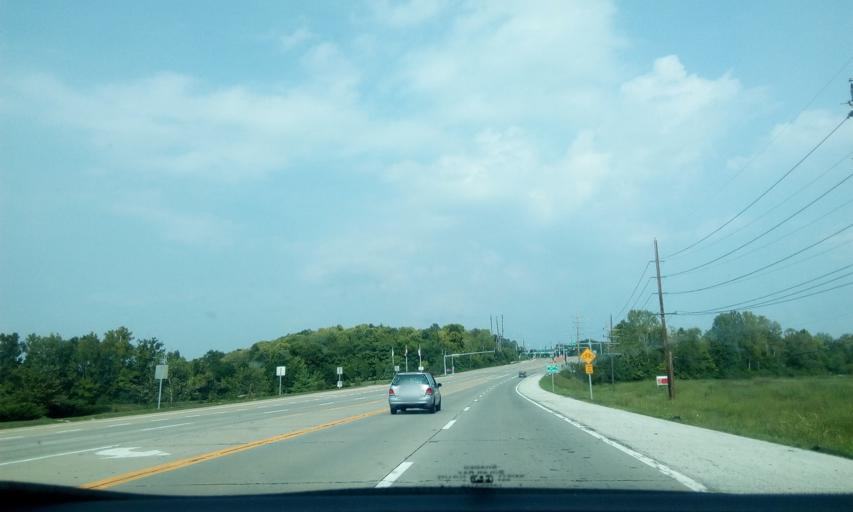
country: US
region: Missouri
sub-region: Saint Louis County
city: Des Peres
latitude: 38.5802
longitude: -90.4534
